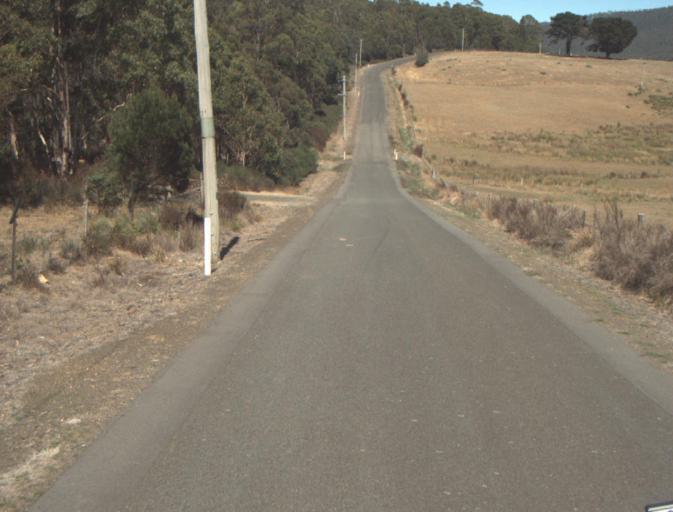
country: AU
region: Tasmania
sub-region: Launceston
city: Newstead
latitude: -41.3164
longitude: 147.3307
